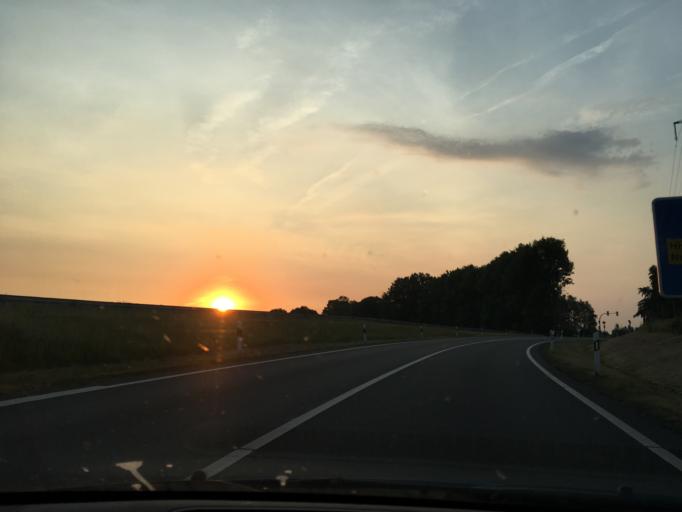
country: DE
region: Lower Saxony
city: Buchholz in der Nordheide
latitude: 53.3728
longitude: 9.8823
